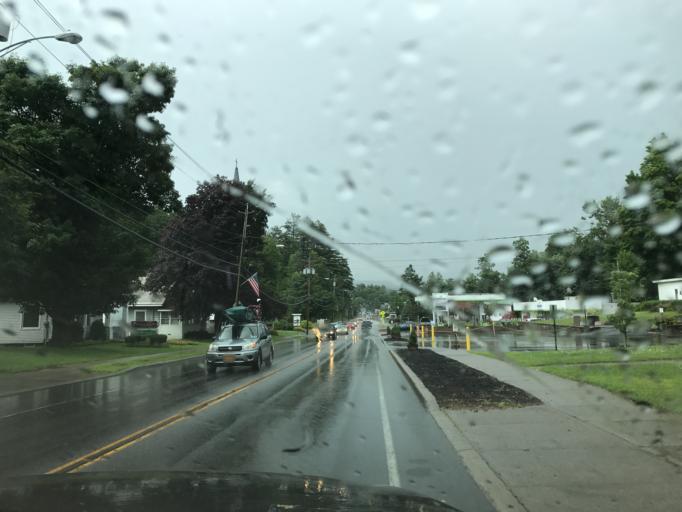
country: US
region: New York
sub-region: Warren County
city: Warrensburg
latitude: 43.4948
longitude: -73.7723
